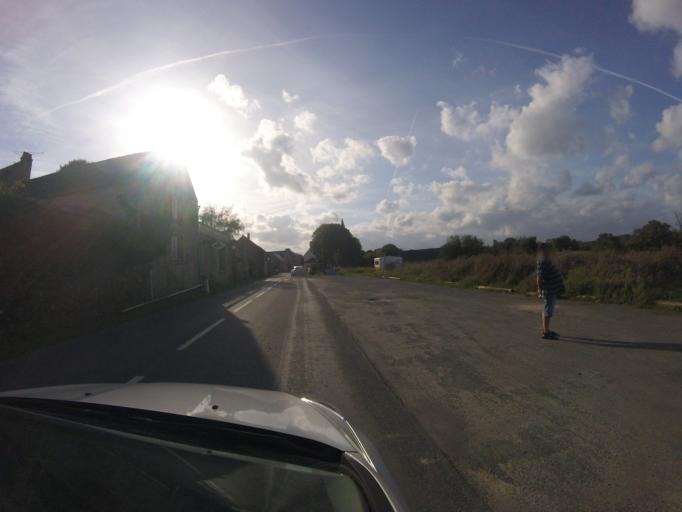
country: FR
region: Lower Normandy
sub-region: Departement du Calvados
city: Port-en-Bessin-Huppain
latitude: 49.3486
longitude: -0.8455
